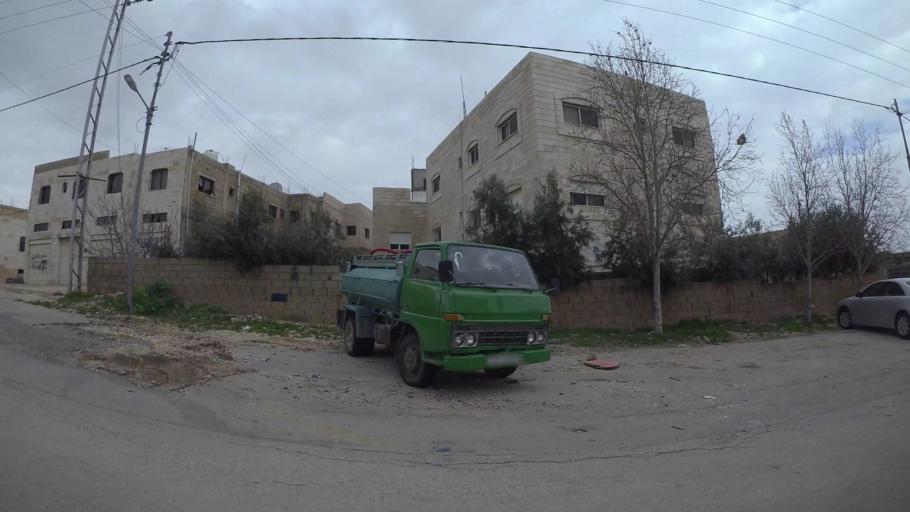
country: JO
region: Amman
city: Wadi as Sir
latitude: 31.9405
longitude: 35.8323
